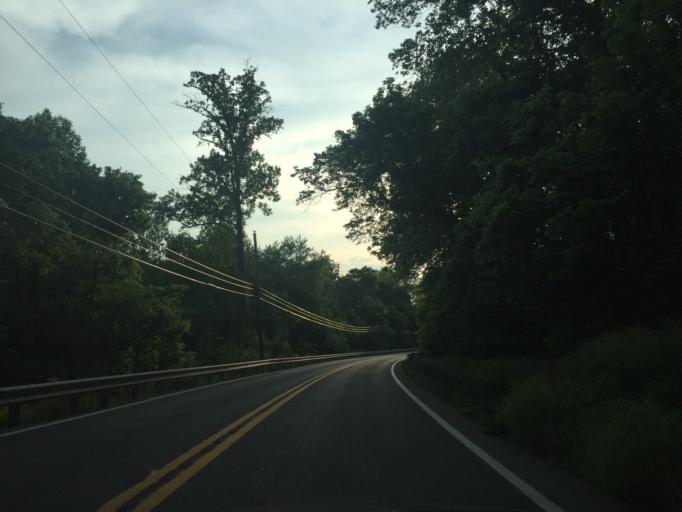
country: US
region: Maryland
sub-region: Frederick County
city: Jefferson
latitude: 39.3312
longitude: -77.5636
